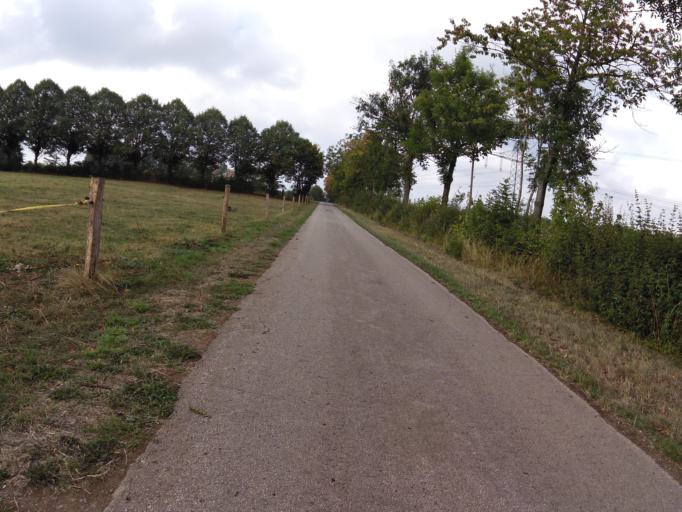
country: DE
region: North Rhine-Westphalia
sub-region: Regierungsbezirk Koln
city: Dahlem
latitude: 50.4181
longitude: 6.5802
